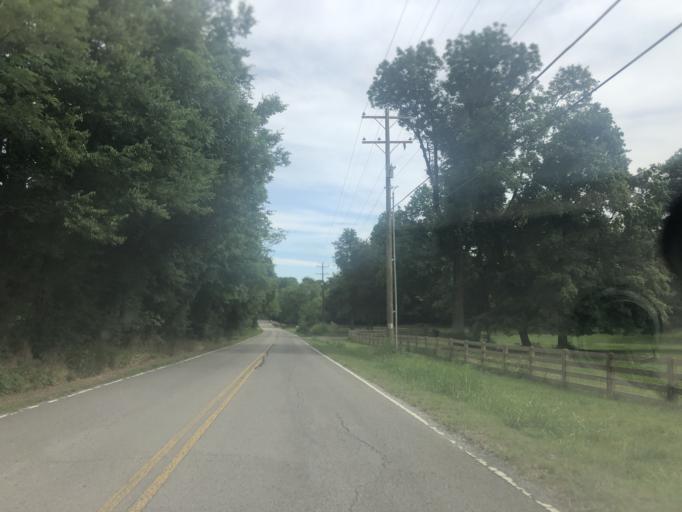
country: US
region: Tennessee
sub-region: Davidson County
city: Lakewood
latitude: 36.2195
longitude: -86.6673
